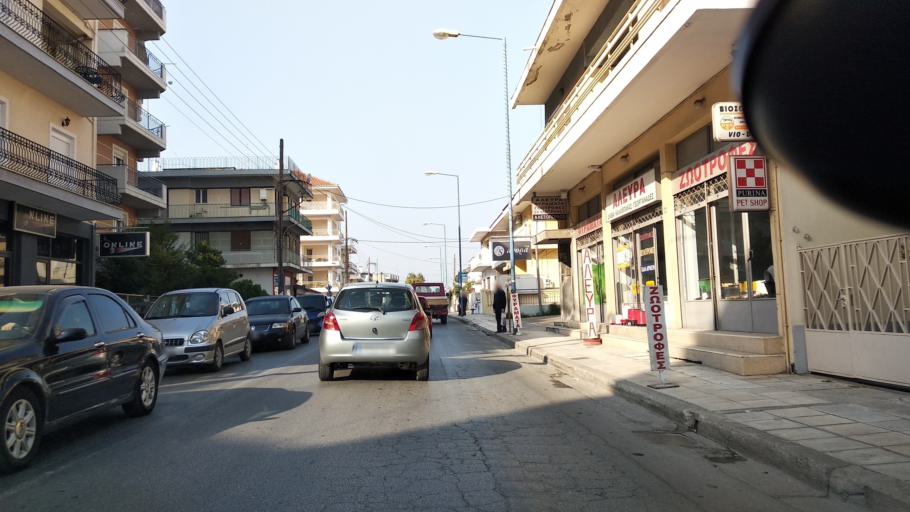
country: GR
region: Thessaly
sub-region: Nomos Larisis
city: Larisa
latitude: 39.6325
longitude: 22.3966
